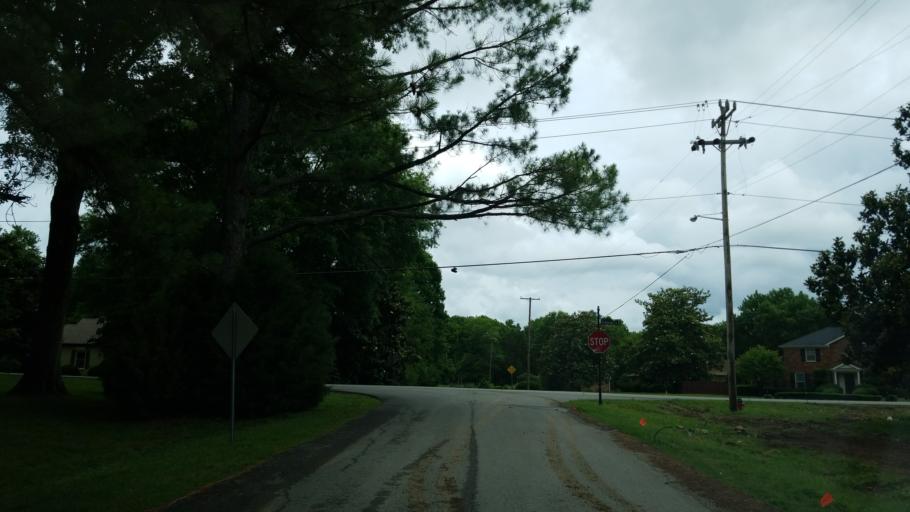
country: US
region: Tennessee
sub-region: Davidson County
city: Forest Hills
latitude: 36.0394
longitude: -86.8315
